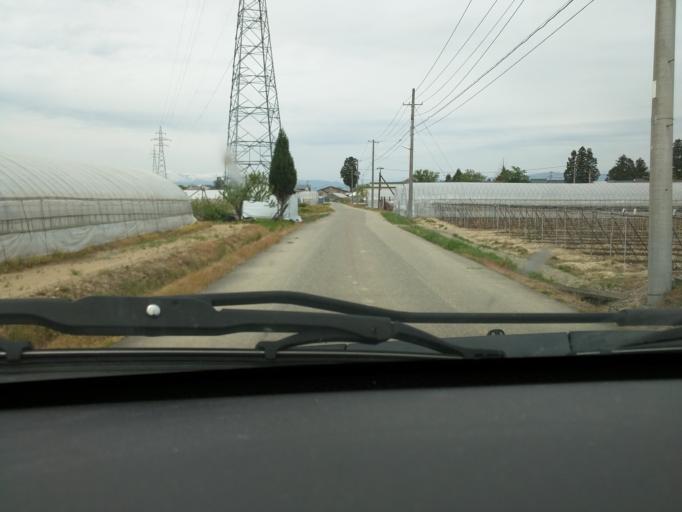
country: JP
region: Fukushima
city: Kitakata
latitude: 37.5212
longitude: 139.8652
